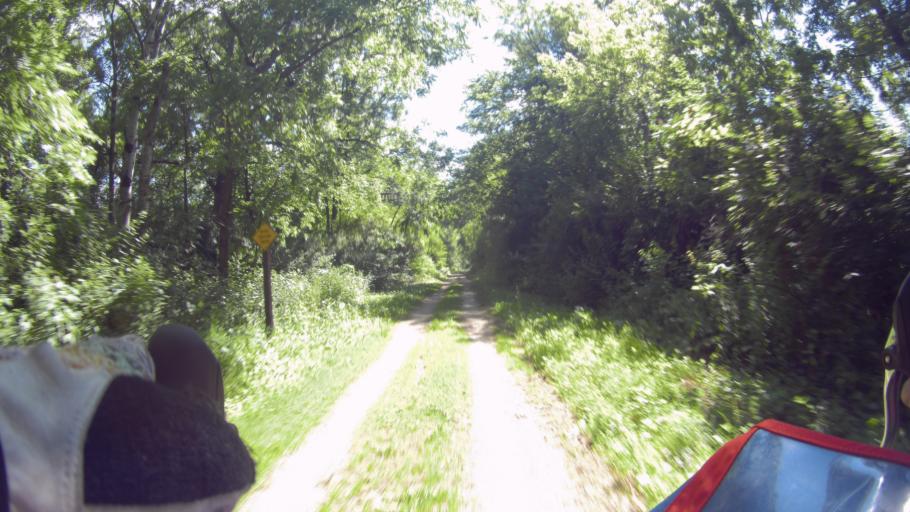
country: US
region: Wisconsin
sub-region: Dane County
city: Fitchburg
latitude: 42.9290
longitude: -89.5051
